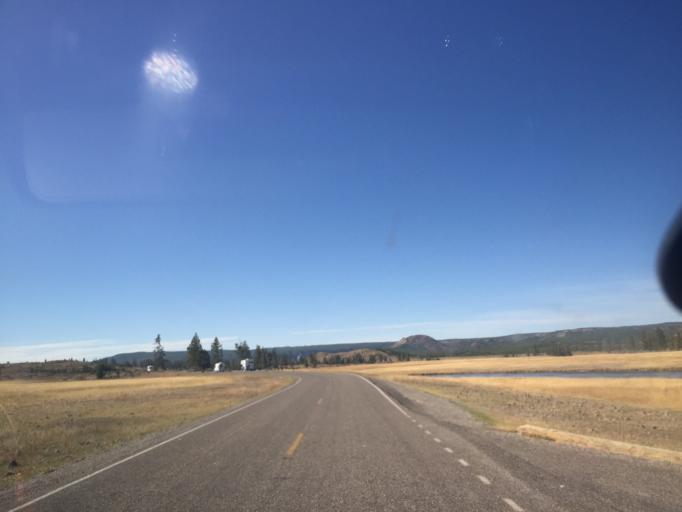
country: US
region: Montana
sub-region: Gallatin County
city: West Yellowstone
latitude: 44.5712
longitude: -110.8327
